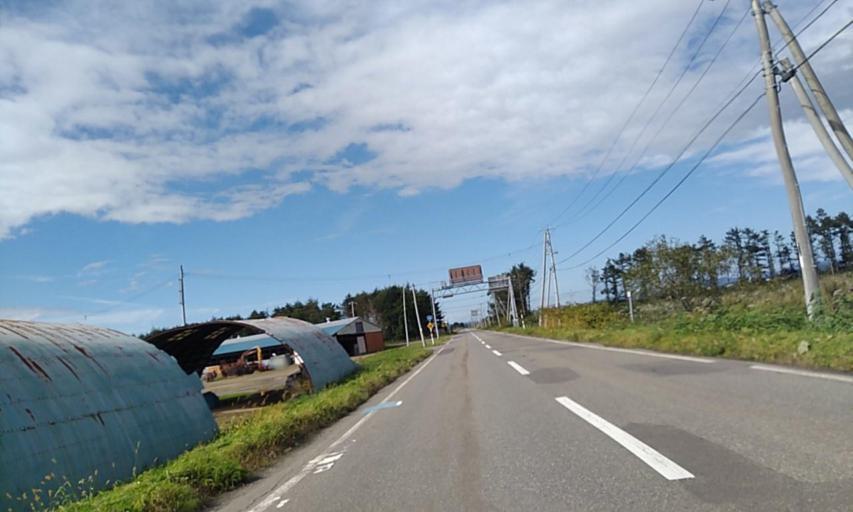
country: JP
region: Hokkaido
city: Obihiro
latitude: 42.7139
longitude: 143.6367
